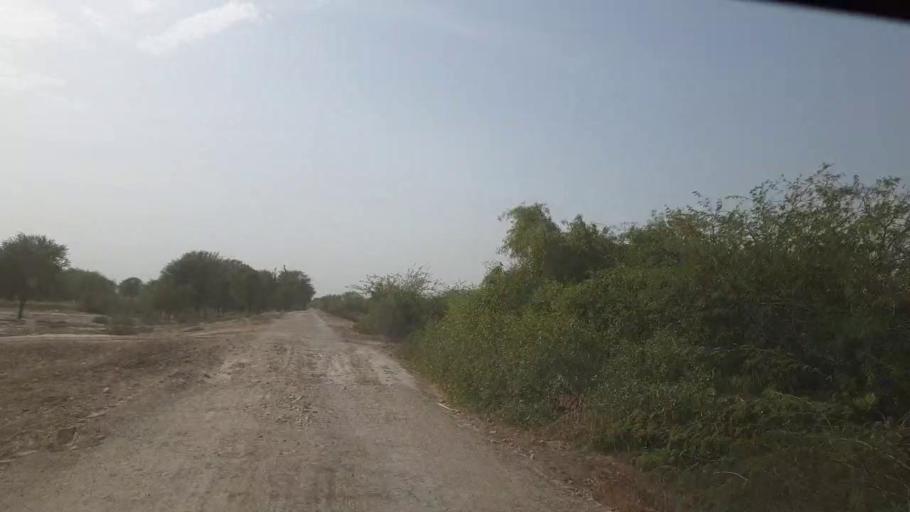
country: PK
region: Sindh
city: Nabisar
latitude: 25.0382
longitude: 69.5045
